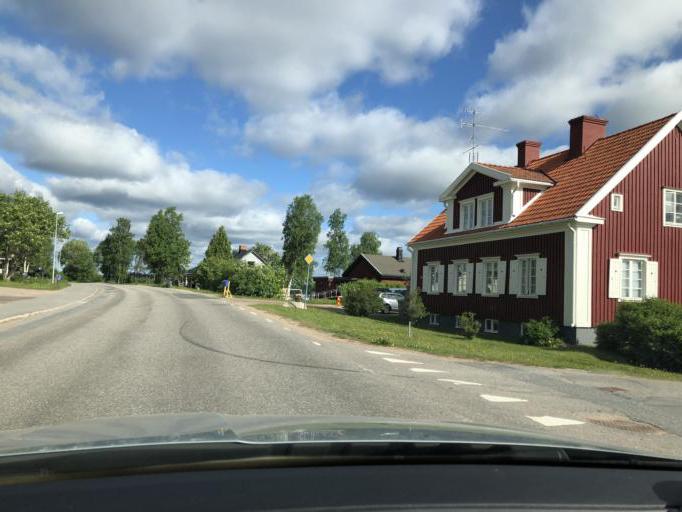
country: SE
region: Norrbotten
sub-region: Pajala Kommun
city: Pajala
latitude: 67.2158
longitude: 23.3652
